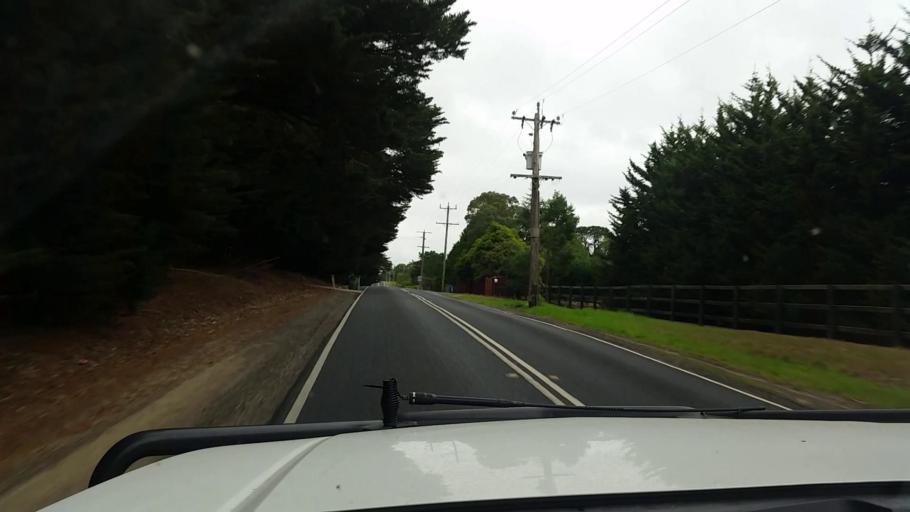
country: AU
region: Victoria
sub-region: Mornington Peninsula
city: Hastings
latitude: -38.2948
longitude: 145.1456
